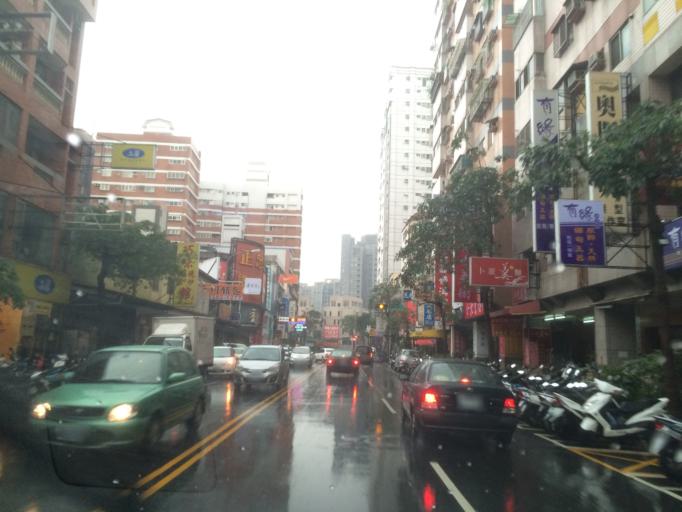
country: TW
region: Taiwan
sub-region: Taichung City
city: Taichung
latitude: 24.1469
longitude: 120.6366
